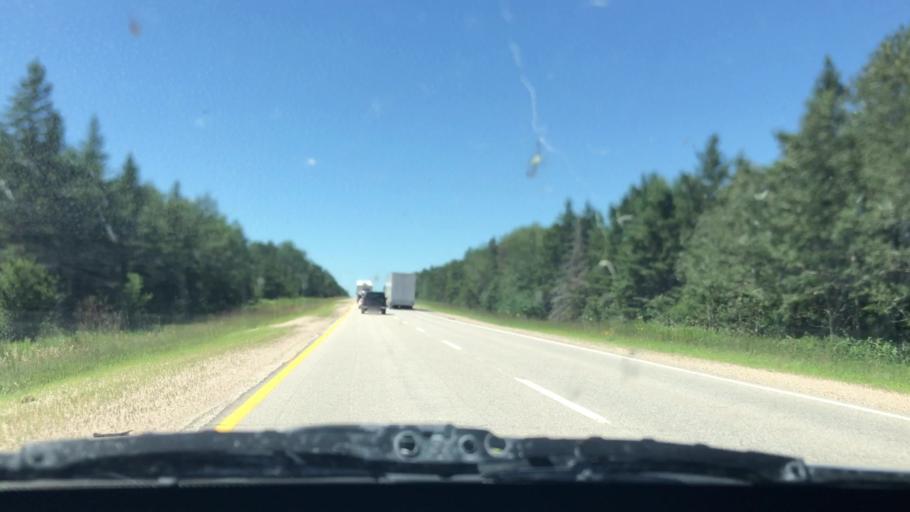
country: CA
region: Manitoba
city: La Broquerie
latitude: 49.6573
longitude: -96.1935
